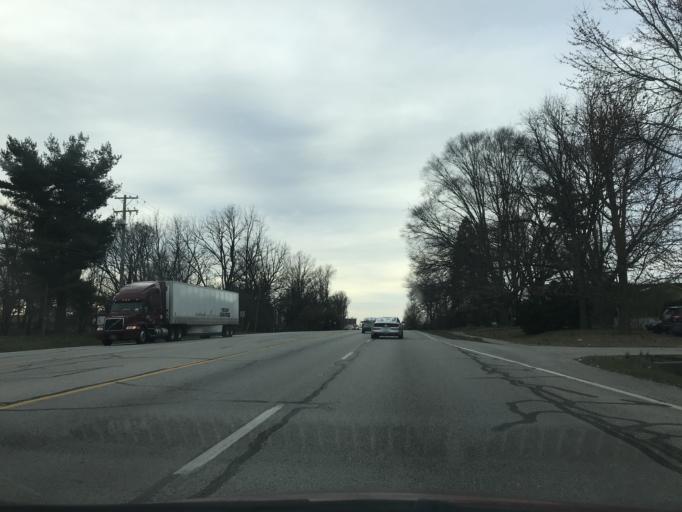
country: US
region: Kentucky
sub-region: Jefferson County
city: West Buechel
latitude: 38.1961
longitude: -85.6800
